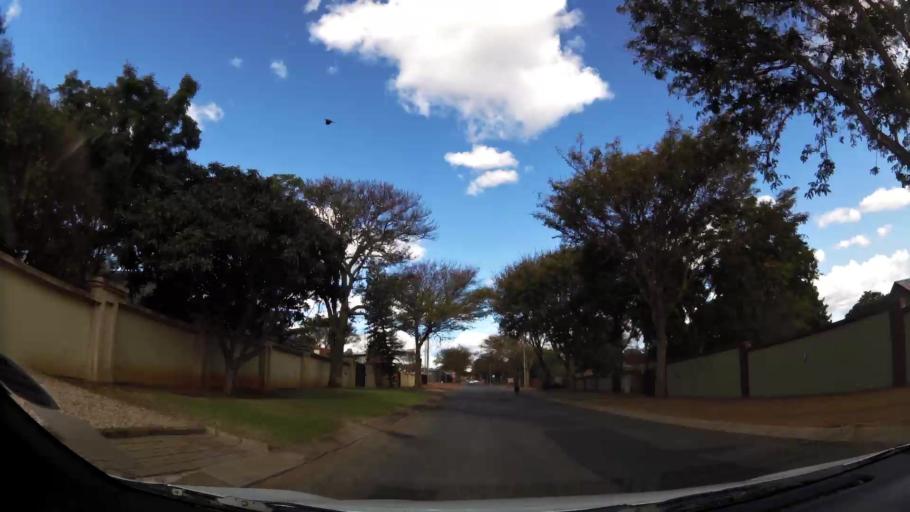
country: ZA
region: Limpopo
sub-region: Capricorn District Municipality
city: Polokwane
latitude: -23.8940
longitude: 29.4824
